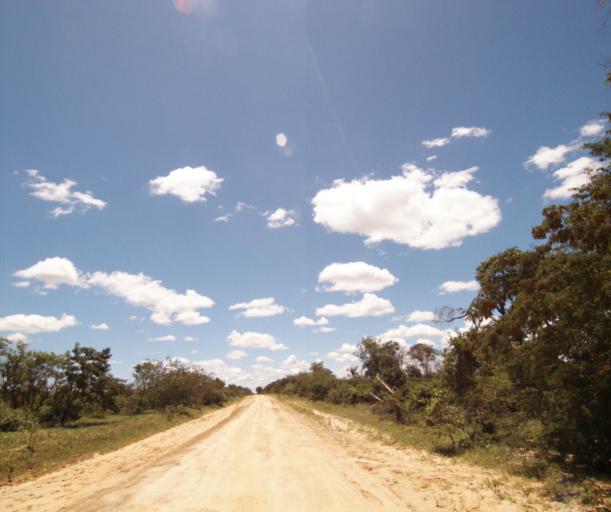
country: BR
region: Bahia
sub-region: Carinhanha
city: Carinhanha
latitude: -14.2097
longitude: -43.9864
